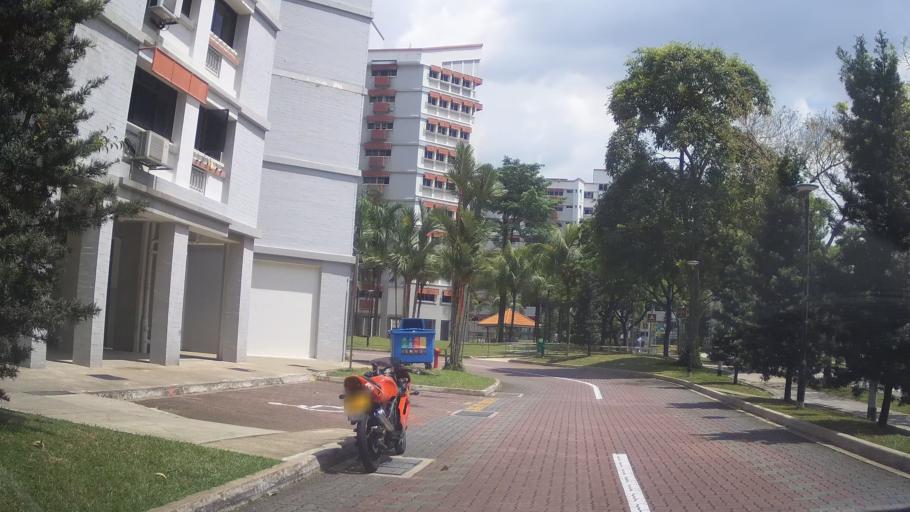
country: MY
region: Johor
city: Johor Bahru
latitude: 1.3372
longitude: 103.7192
